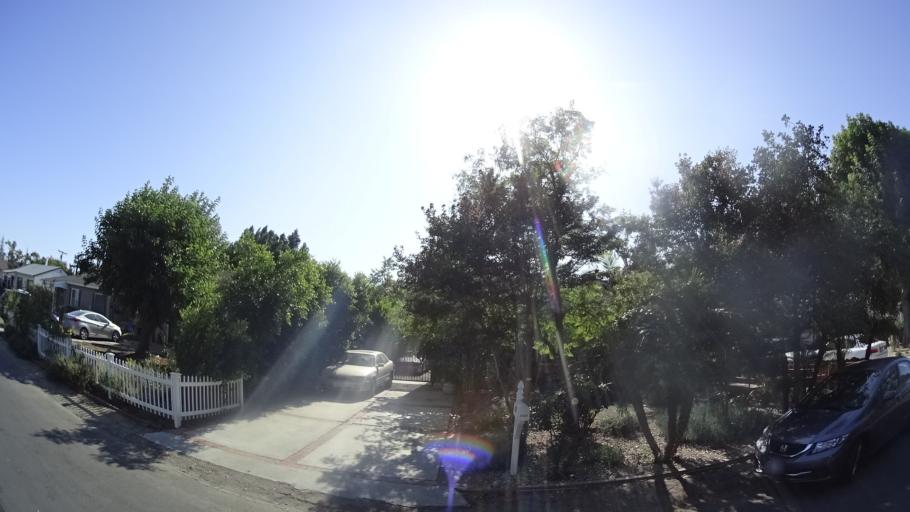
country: US
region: California
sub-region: Los Angeles County
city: Van Nuys
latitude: 34.1777
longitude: -118.4520
